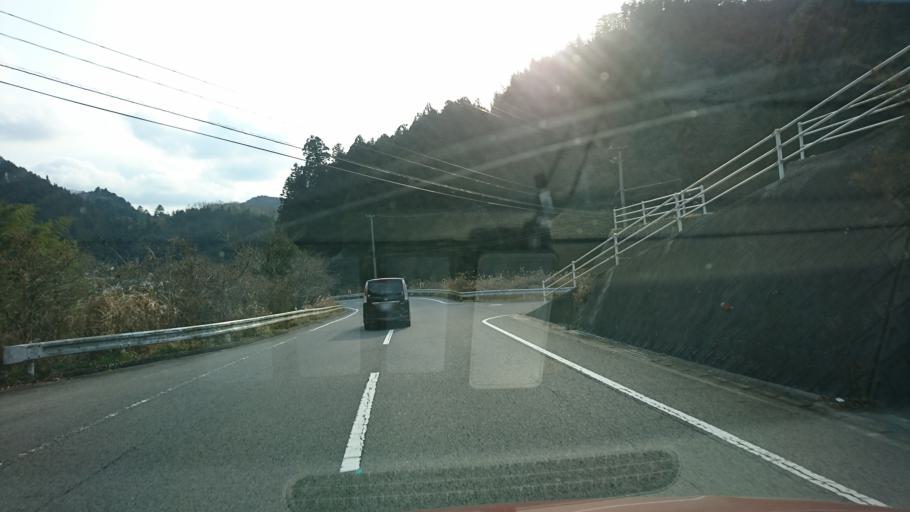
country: JP
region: Ehime
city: Hojo
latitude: 33.9207
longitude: 132.8861
